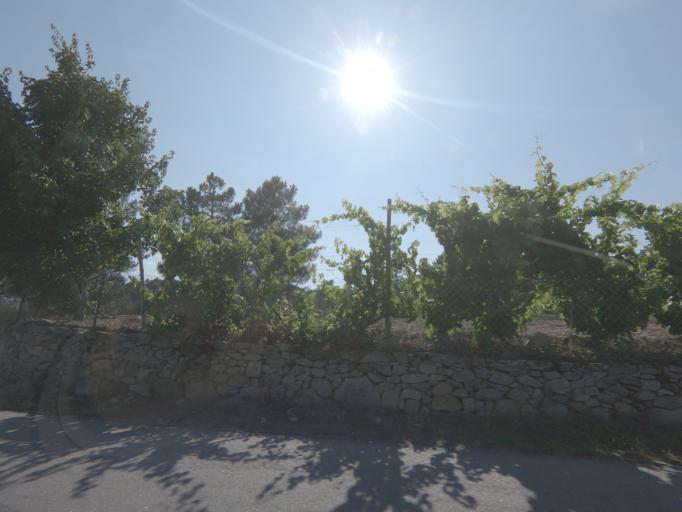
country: PT
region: Viseu
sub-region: Moimenta da Beira
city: Moimenta da Beira
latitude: 40.9968
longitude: -7.5586
